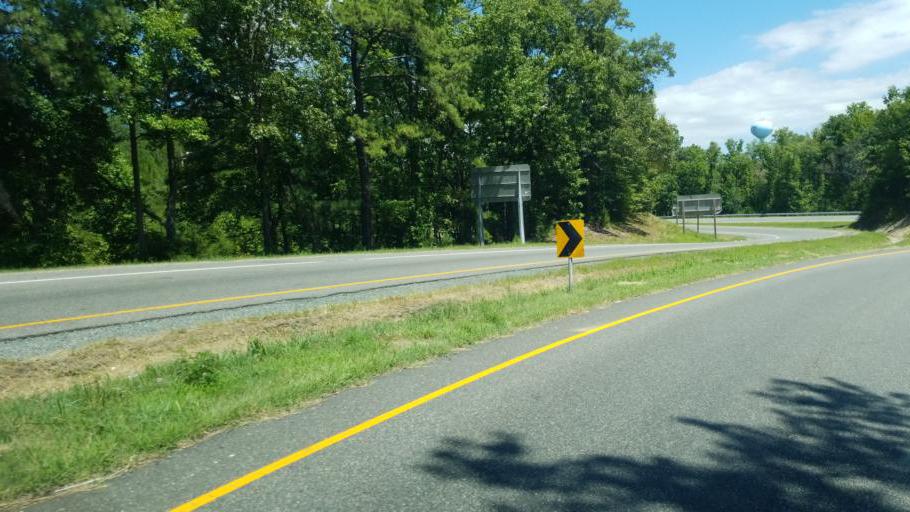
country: US
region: Virginia
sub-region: Caroline County
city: Bowling Green
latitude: 37.9365
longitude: -77.4730
